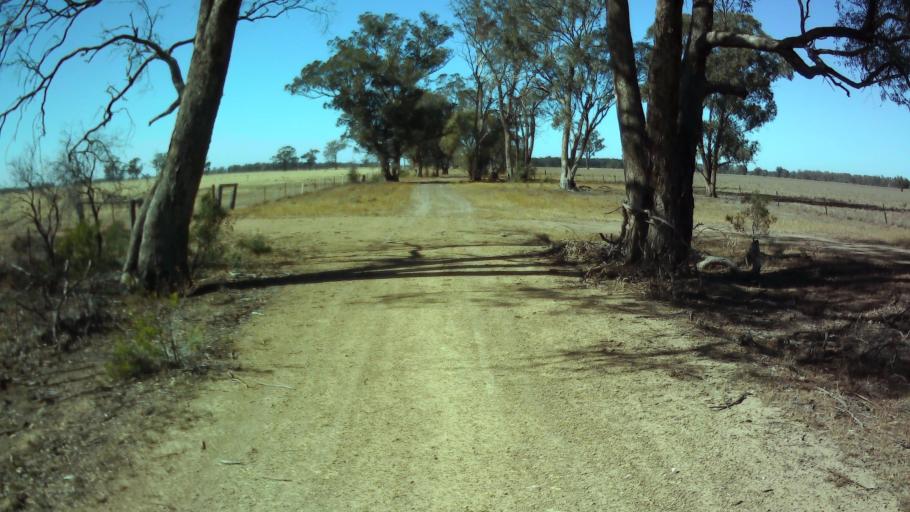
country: AU
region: New South Wales
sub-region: Weddin
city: Grenfell
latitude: -33.9464
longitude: 147.8700
